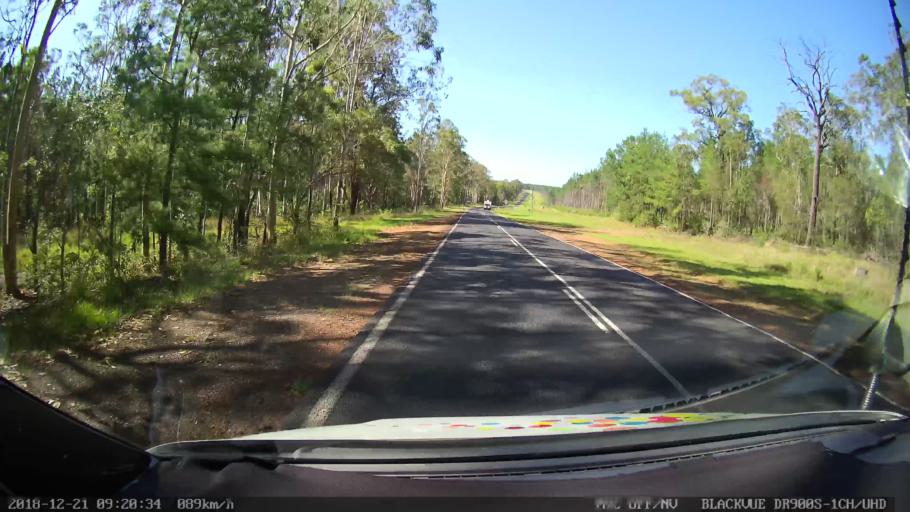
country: AU
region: New South Wales
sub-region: Clarence Valley
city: Maclean
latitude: -29.3165
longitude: 153.0003
